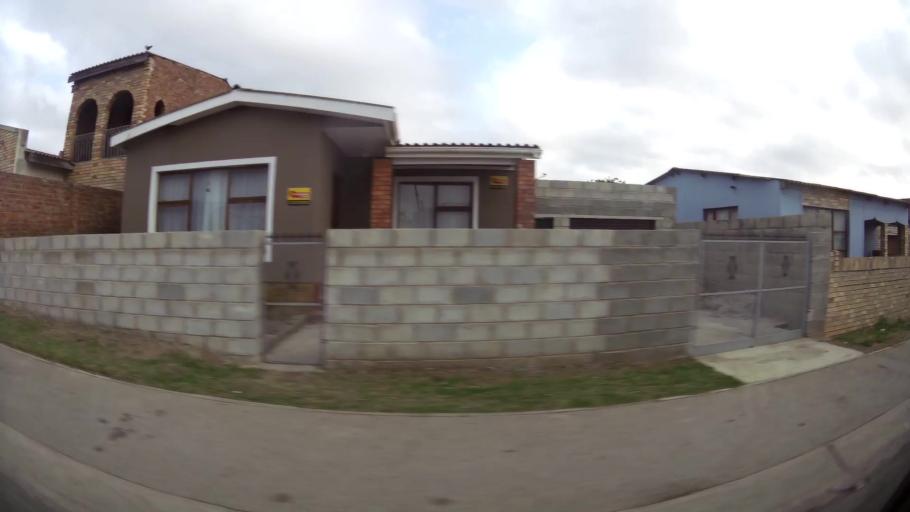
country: ZA
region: Eastern Cape
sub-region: Nelson Mandela Bay Metropolitan Municipality
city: Port Elizabeth
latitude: -33.9188
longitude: 25.5548
